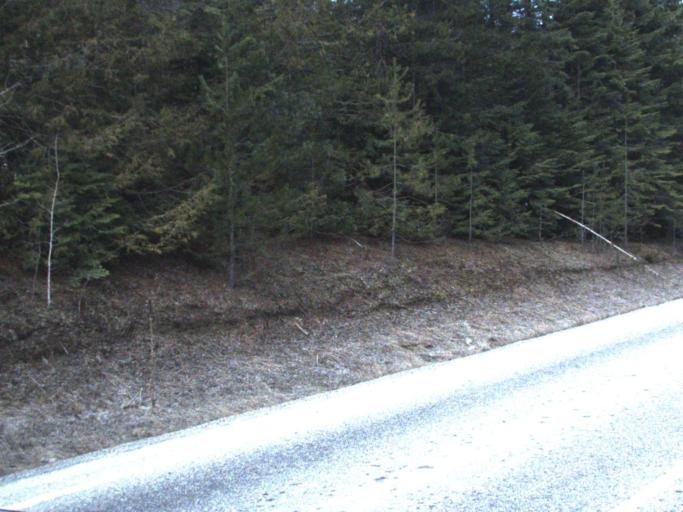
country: US
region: Washington
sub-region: Stevens County
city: Chewelah
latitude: 48.5948
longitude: -117.3559
